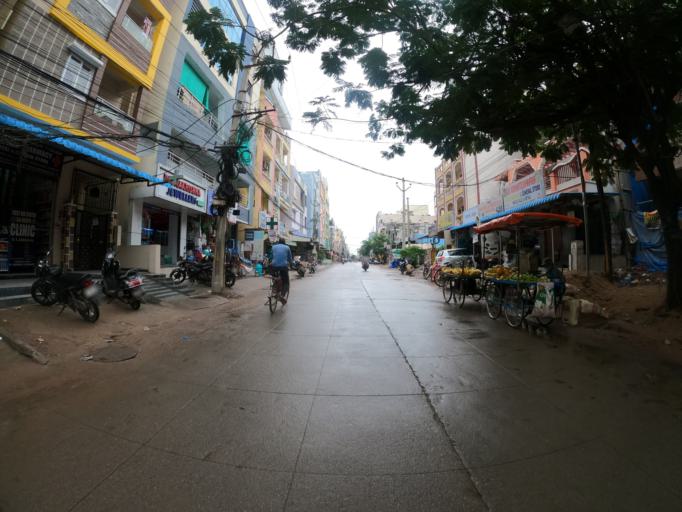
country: IN
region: Telangana
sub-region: Rangareddi
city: Kukatpalli
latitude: 17.4594
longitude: 78.4009
